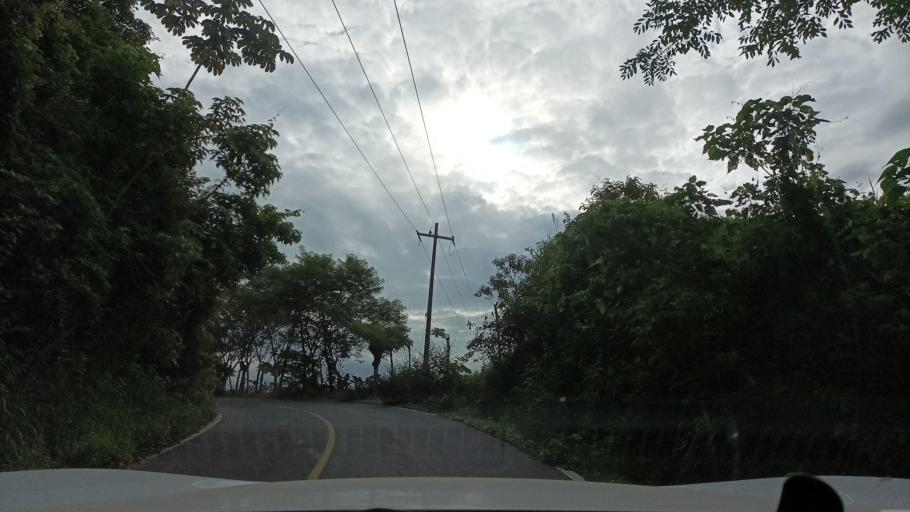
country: MX
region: Veracruz
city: Hidalgotitlan
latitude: 17.6902
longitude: -94.4540
